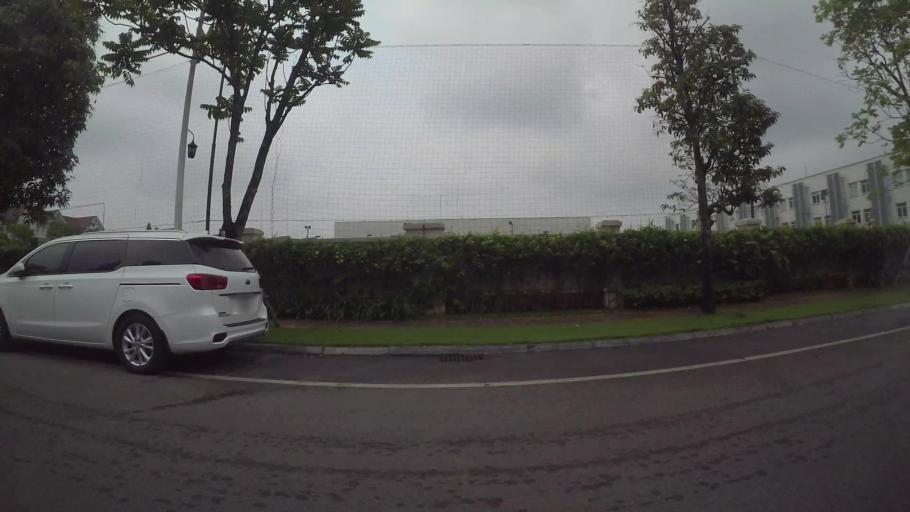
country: VN
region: Ha Noi
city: Trau Quy
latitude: 21.0439
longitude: 105.9198
